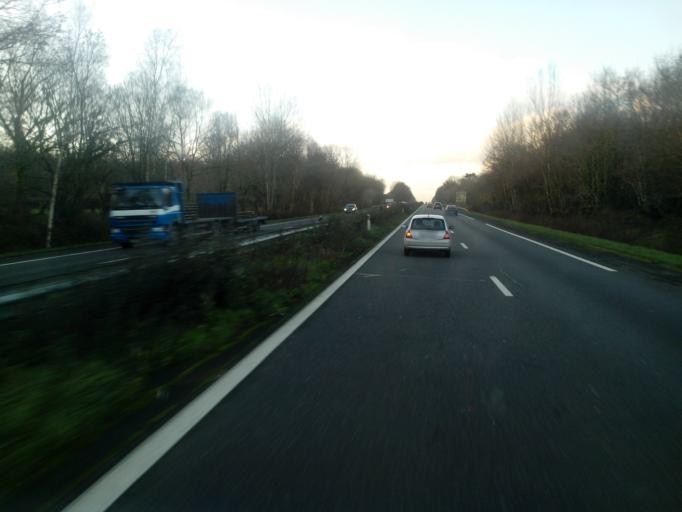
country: FR
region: Pays de la Loire
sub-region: Departement de la Loire-Atlantique
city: Haute-Goulaine
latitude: 47.1862
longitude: -1.4217
